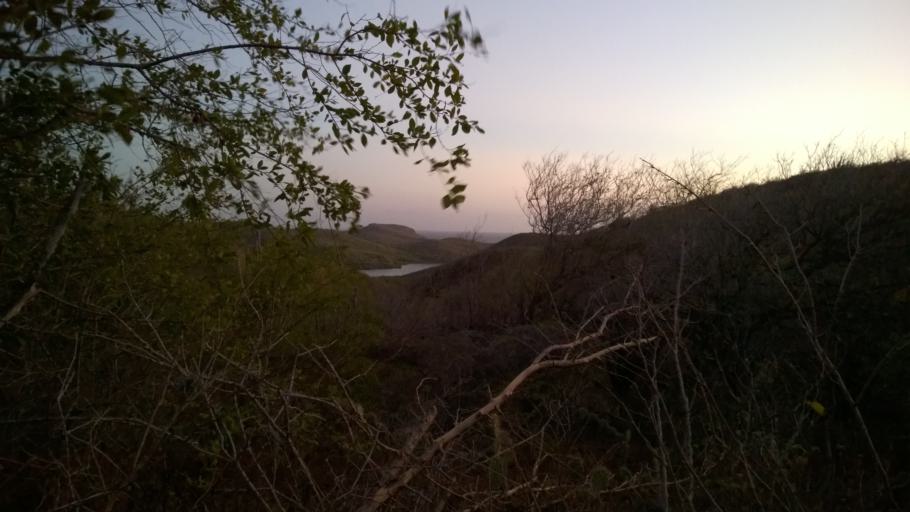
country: CW
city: Dorp Soto
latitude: 12.2628
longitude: -69.1063
